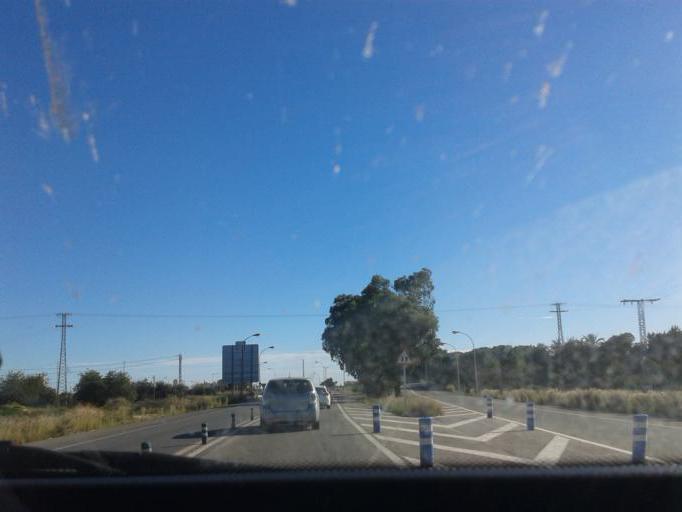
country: ES
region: Valencia
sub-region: Provincia de Alicante
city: San Juan de Alicante
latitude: 38.4162
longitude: -0.4233
